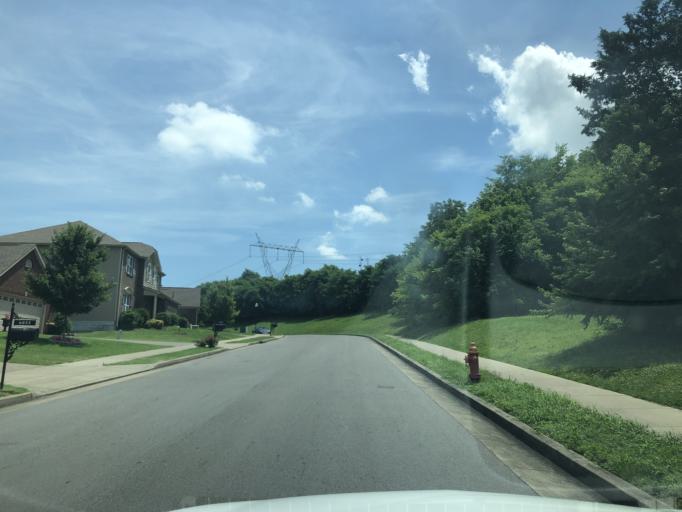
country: US
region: Tennessee
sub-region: Rutherford County
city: La Vergne
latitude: 36.0220
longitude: -86.6415
